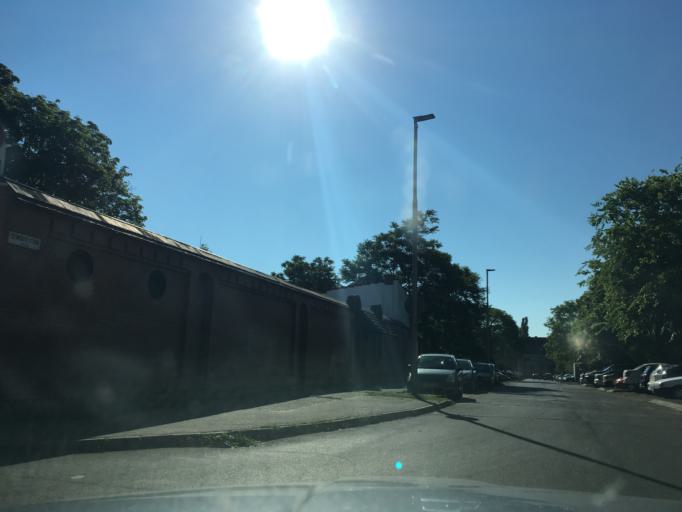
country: HU
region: Hajdu-Bihar
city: Debrecen
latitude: 47.5267
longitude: 21.6332
